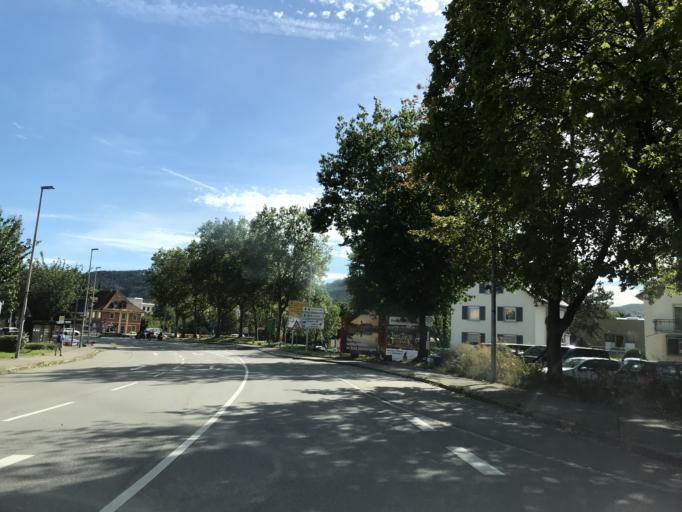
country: DE
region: Baden-Wuerttemberg
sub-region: Freiburg Region
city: Bad Sackingen
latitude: 47.5587
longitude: 7.9456
